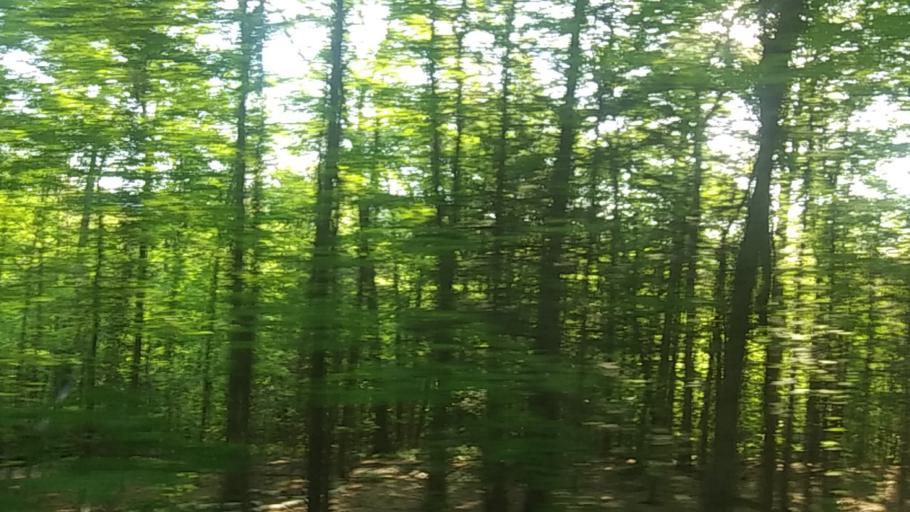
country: US
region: Massachusetts
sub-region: Franklin County
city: Shelburne Falls
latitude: 42.5913
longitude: -72.7456
